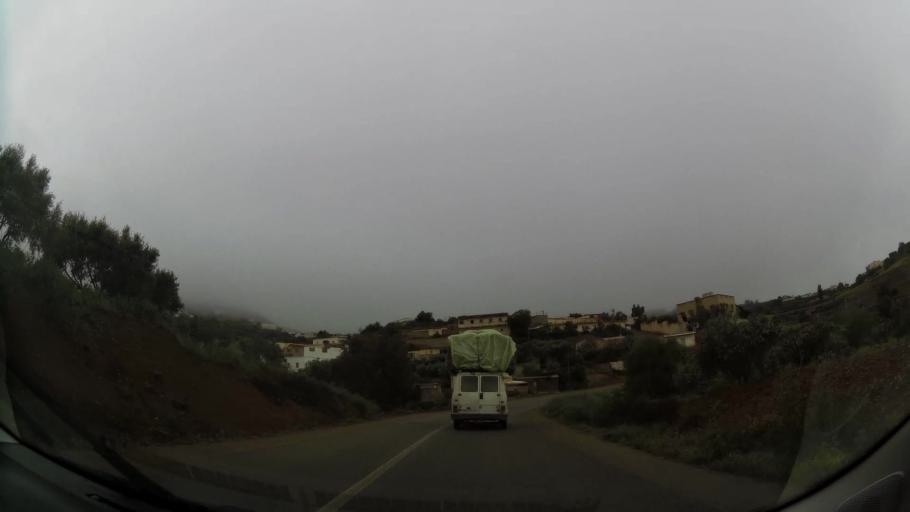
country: MA
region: Oriental
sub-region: Nador
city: Boudinar
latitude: 35.0899
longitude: -3.5235
